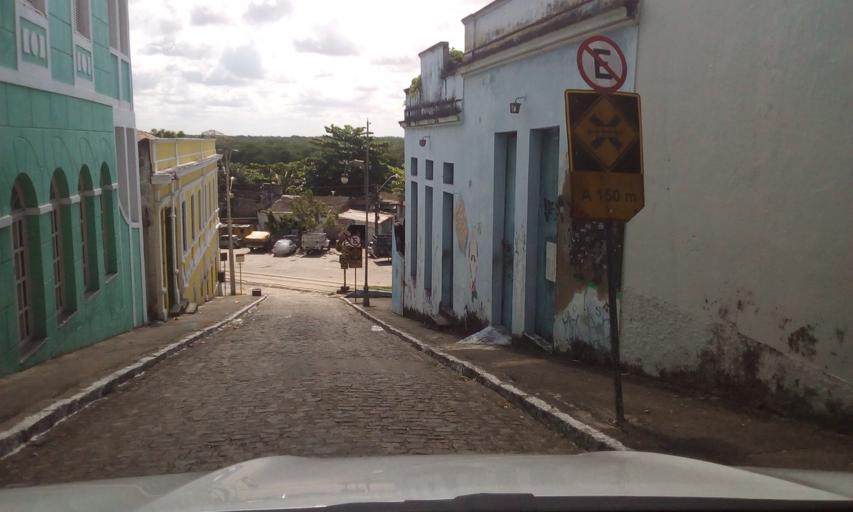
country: BR
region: Paraiba
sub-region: Joao Pessoa
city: Joao Pessoa
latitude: -7.1126
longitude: -34.8890
